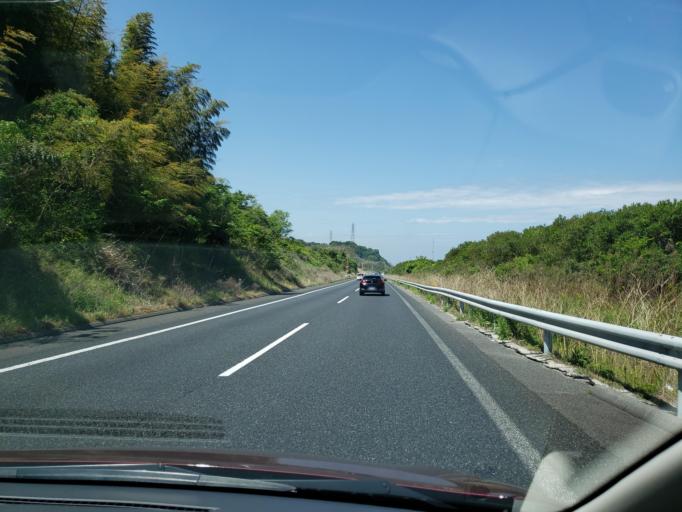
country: JP
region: Hyogo
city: Akashi
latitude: 34.5289
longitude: 134.9255
